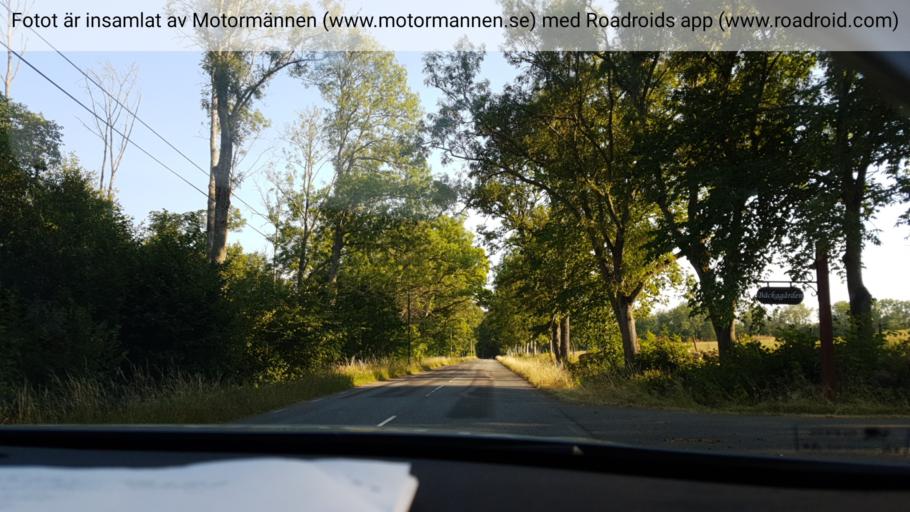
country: SE
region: Vaestra Goetaland
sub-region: Skovde Kommun
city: Stopen
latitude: 58.4735
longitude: 13.8389
